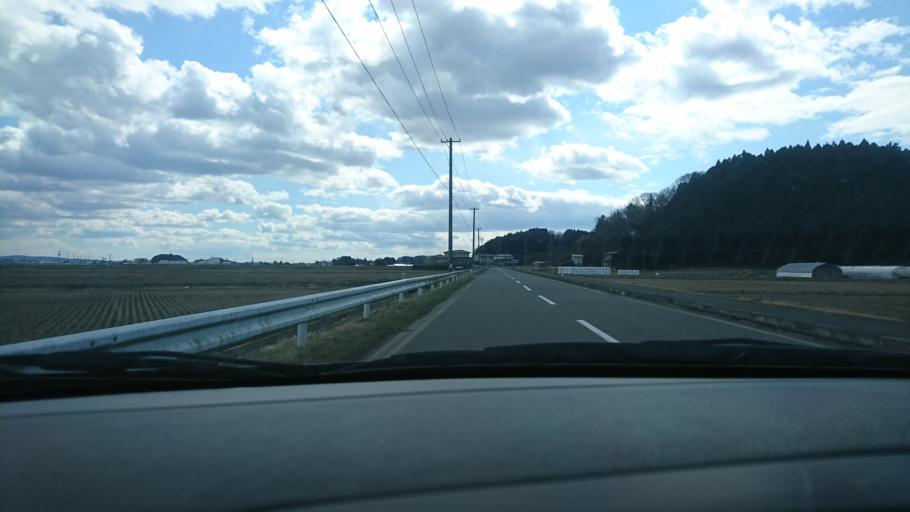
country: JP
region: Iwate
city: Ichinoseki
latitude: 38.7522
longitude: 141.2283
